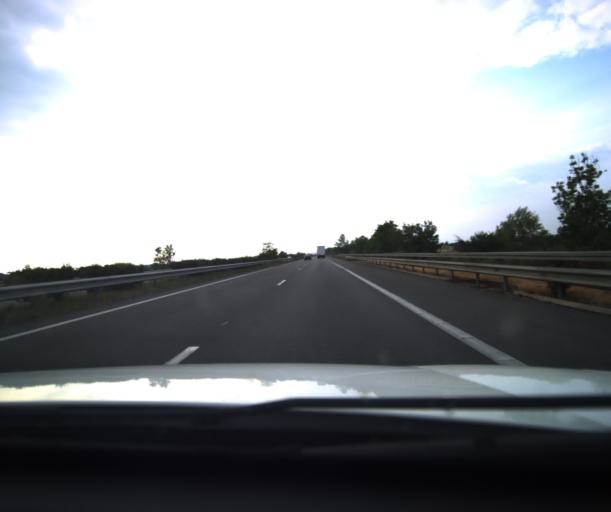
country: FR
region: Midi-Pyrenees
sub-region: Departement du Tarn-et-Garonne
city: Saint-Porquier
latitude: 44.0364
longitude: 1.1557
